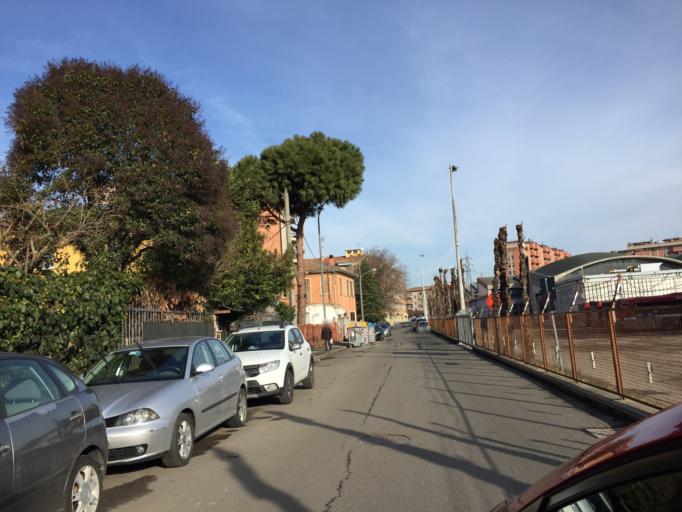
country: IT
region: Emilia-Romagna
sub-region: Provincia di Bologna
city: Casalecchio di Reno
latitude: 44.5015
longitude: 11.2946
